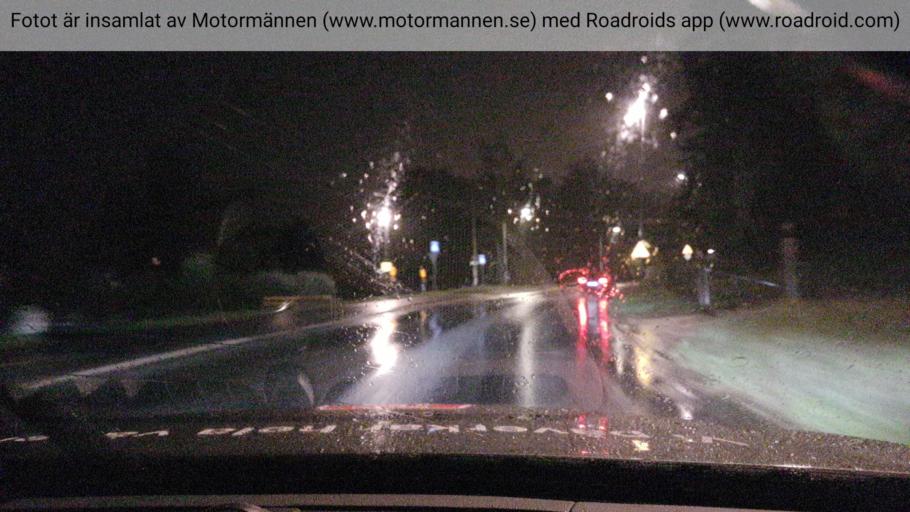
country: SE
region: Stockholm
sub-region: Haninge Kommun
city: Haninge
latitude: 59.1870
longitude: 18.1845
